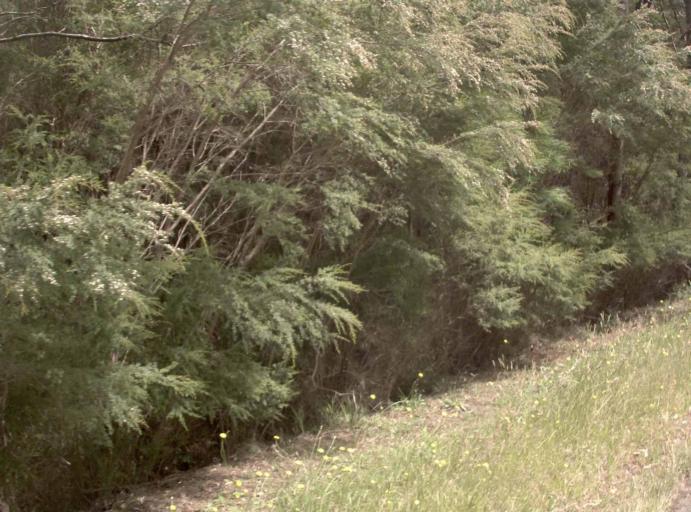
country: AU
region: Victoria
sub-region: Latrobe
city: Moe
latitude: -37.9391
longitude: 146.4025
